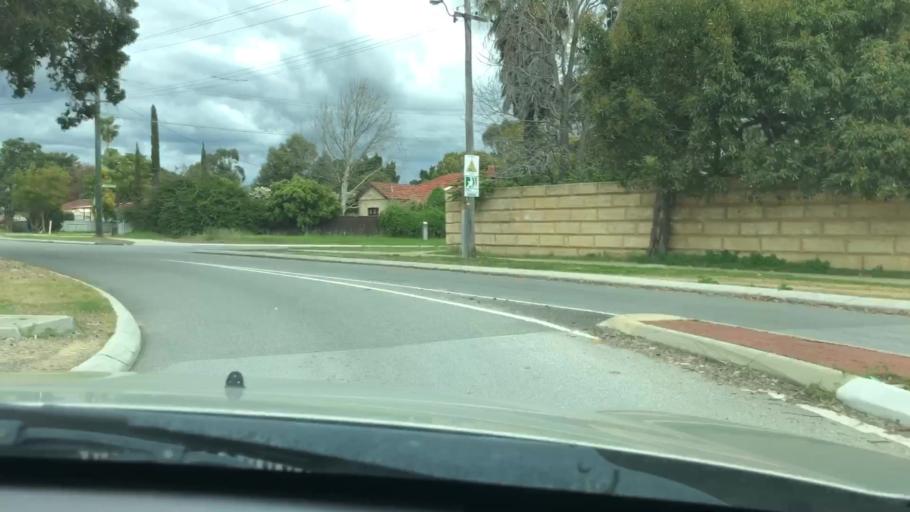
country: AU
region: Western Australia
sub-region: Armadale
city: Seville Grove
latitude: -32.1472
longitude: 115.9959
